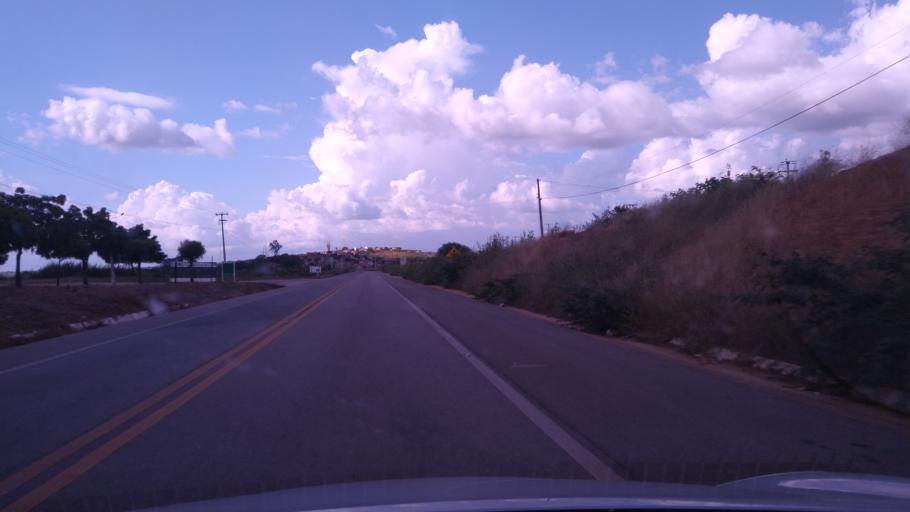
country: BR
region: Ceara
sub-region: Caninde
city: Caninde
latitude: -4.3821
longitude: -39.3106
